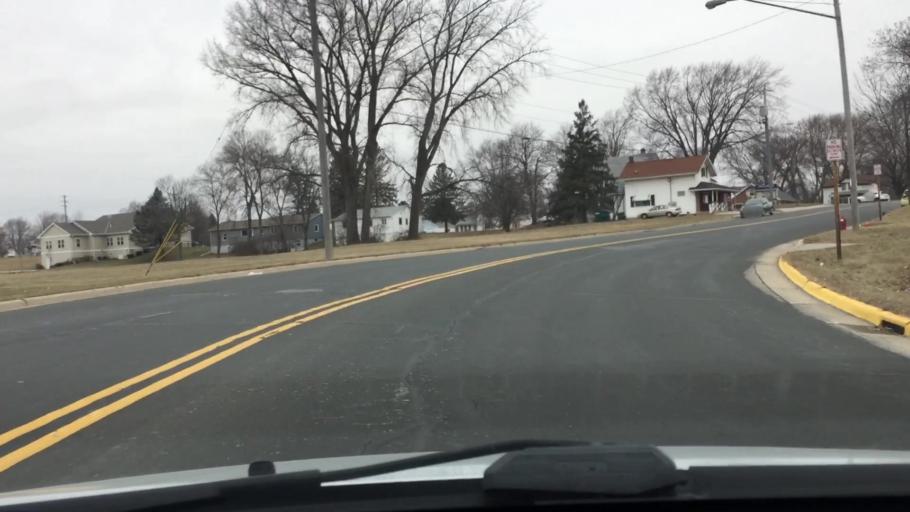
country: US
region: Wisconsin
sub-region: Jefferson County
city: Watertown
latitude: 43.1867
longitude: -88.7322
